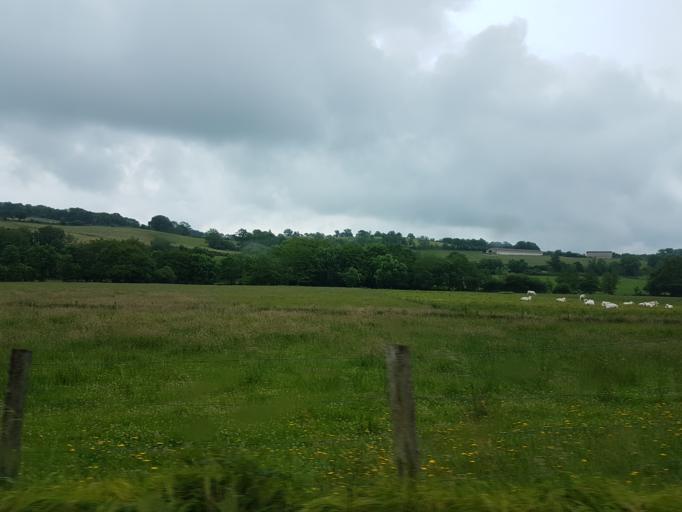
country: FR
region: Bourgogne
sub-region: Departement de la Nievre
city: Lormes
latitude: 47.1811
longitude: 3.7901
